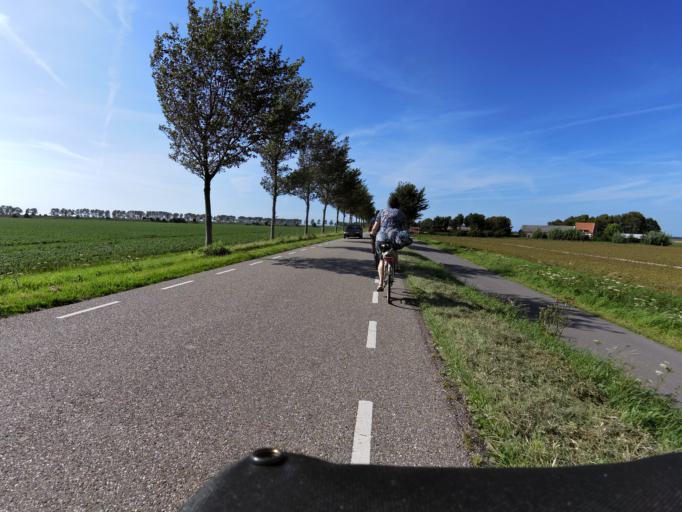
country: NL
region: South Holland
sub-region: Gemeente Goeree-Overflakkee
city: Dirksland
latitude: 51.7290
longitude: 4.0746
